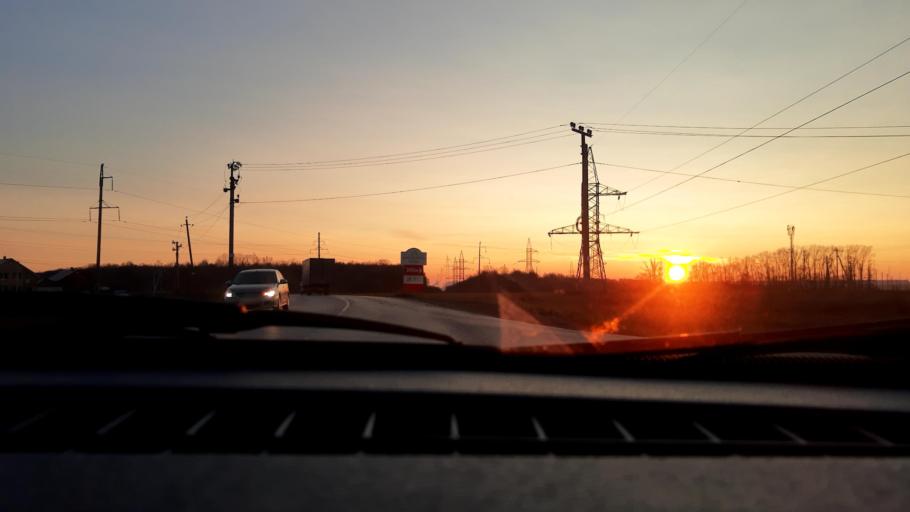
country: RU
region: Bashkortostan
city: Mikhaylovka
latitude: 54.8296
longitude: 55.8858
